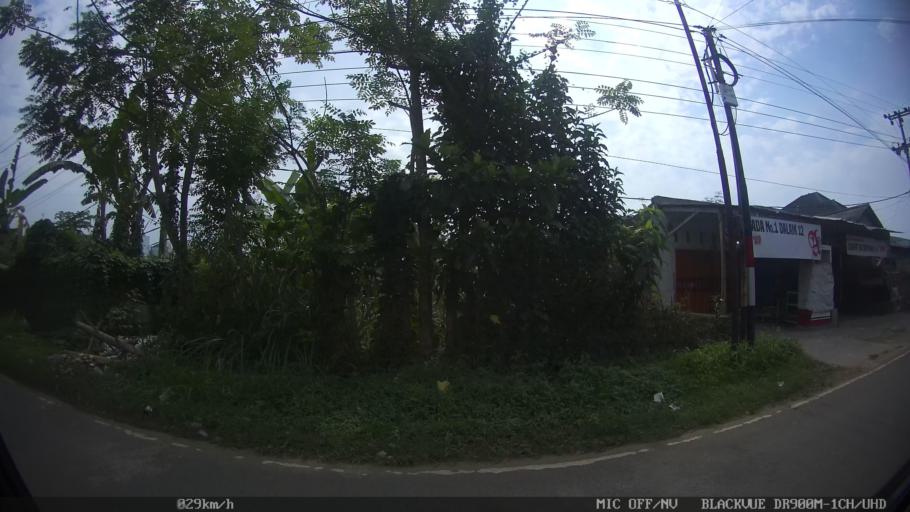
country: ID
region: Lampung
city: Bandarlampung
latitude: -5.4531
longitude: 105.2436
